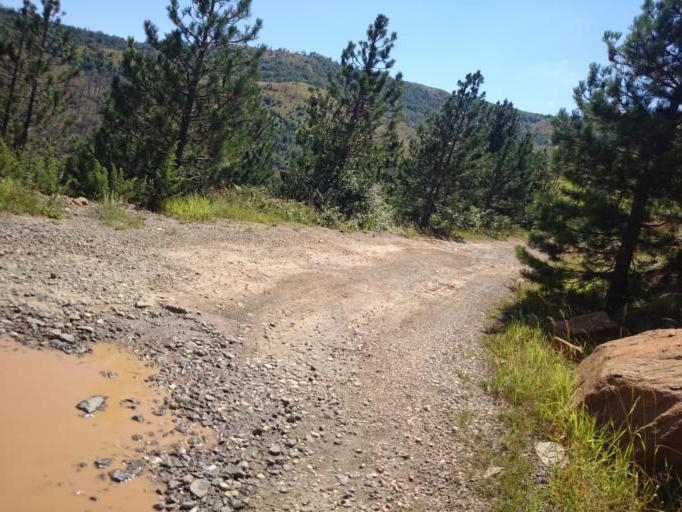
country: AL
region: Diber
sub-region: Rrethi i Bulqizes
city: Zerqan
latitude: 41.4260
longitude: 20.3235
